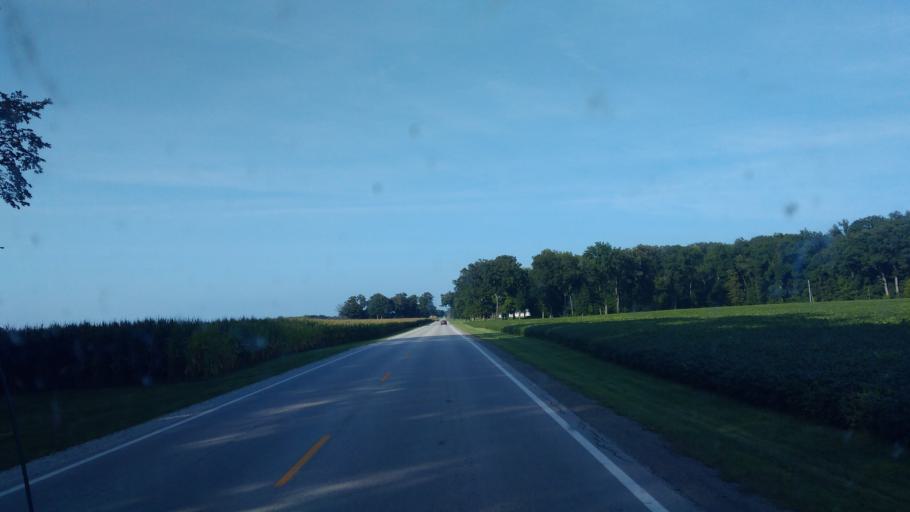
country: US
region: Ohio
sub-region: Wyandot County
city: Upper Sandusky
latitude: 40.8774
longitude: -83.2500
